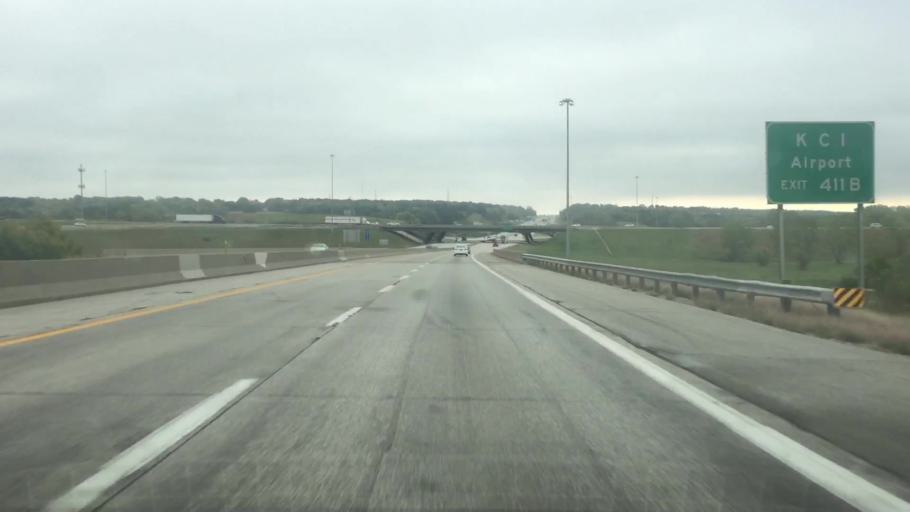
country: US
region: Kansas
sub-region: Wyandotte County
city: Edwardsville
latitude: 39.1059
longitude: -94.8161
